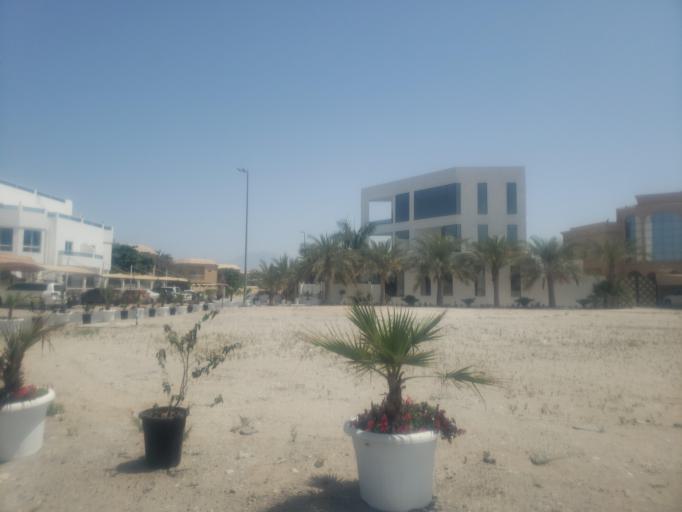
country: AE
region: Ra's al Khaymah
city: Ras al-Khaimah
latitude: 25.8106
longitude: 55.9553
